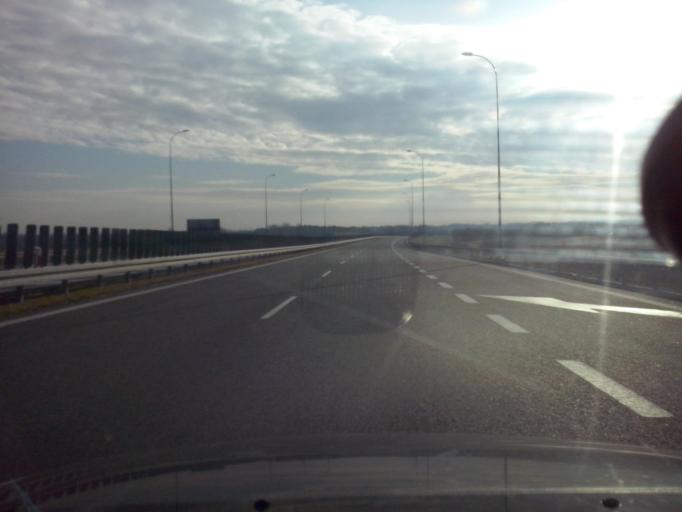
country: PL
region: Subcarpathian Voivodeship
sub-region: Powiat rzeszowski
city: Rudna Wielka
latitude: 50.1003
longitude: 21.9303
